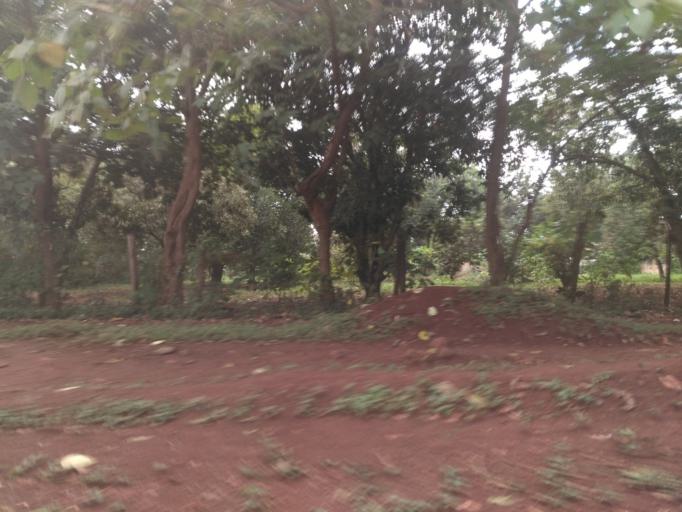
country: UG
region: Central Region
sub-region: Buikwe District
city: Njeru
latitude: 0.4251
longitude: 33.1897
